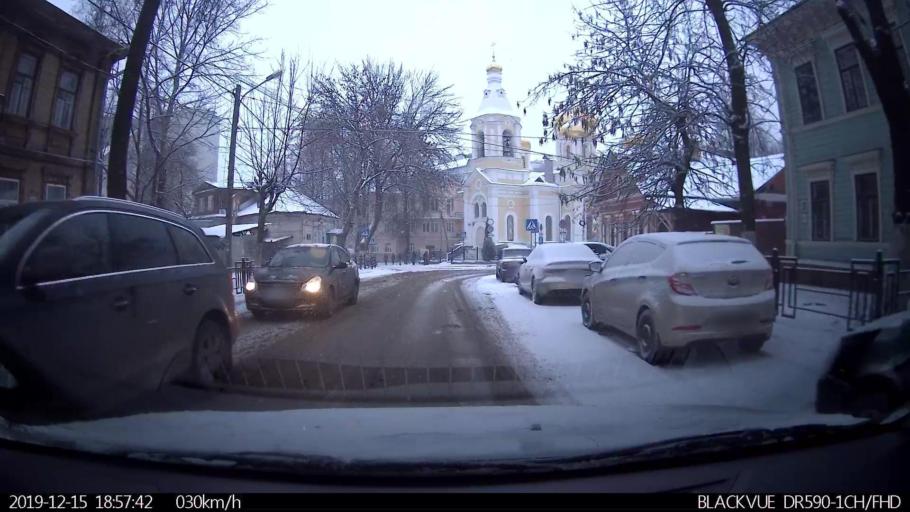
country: RU
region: Nizjnij Novgorod
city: Nizhniy Novgorod
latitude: 56.3123
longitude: 43.9963
